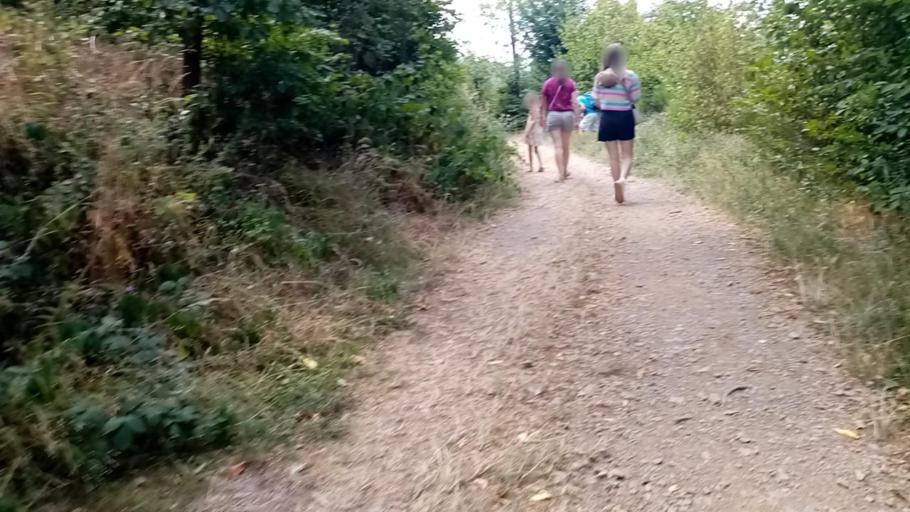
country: FR
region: Rhone-Alpes
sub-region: Departement du Rhone
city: Grandris
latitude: 46.0115
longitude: 4.5446
